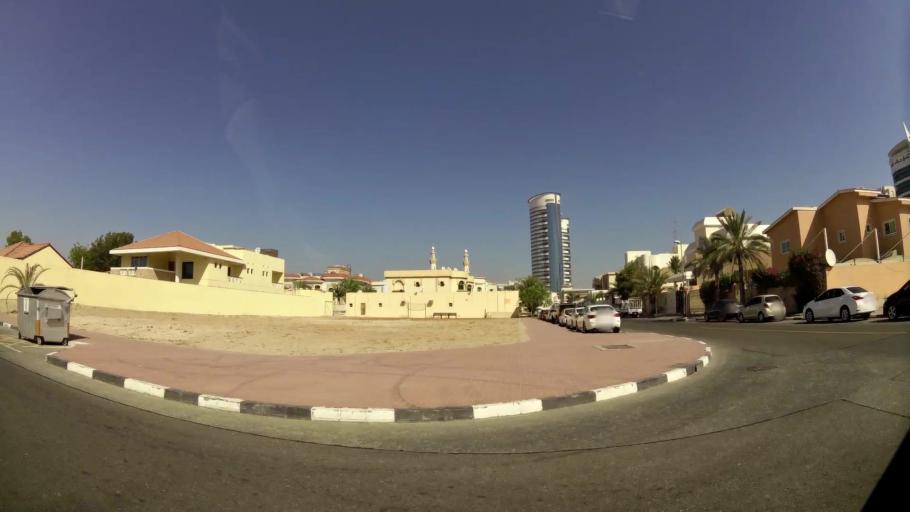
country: AE
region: Ash Shariqah
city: Sharjah
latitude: 25.2493
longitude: 55.2923
